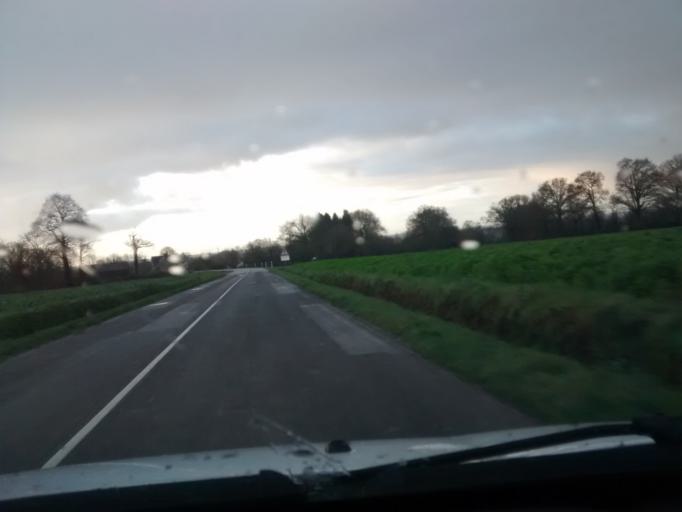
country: FR
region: Brittany
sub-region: Departement d'Ille-et-Vilaine
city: Bais
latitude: 47.9889
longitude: -1.2860
